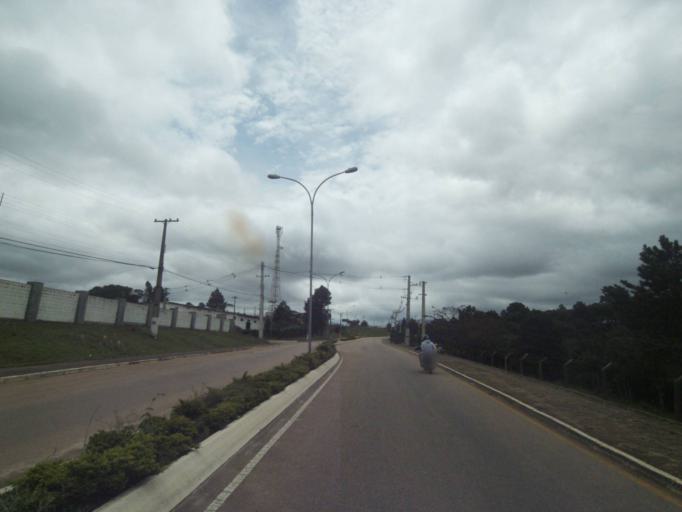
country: BR
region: Parana
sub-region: Campina Grande Do Sul
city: Campina Grande do Sul
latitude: -25.3084
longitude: -49.0603
